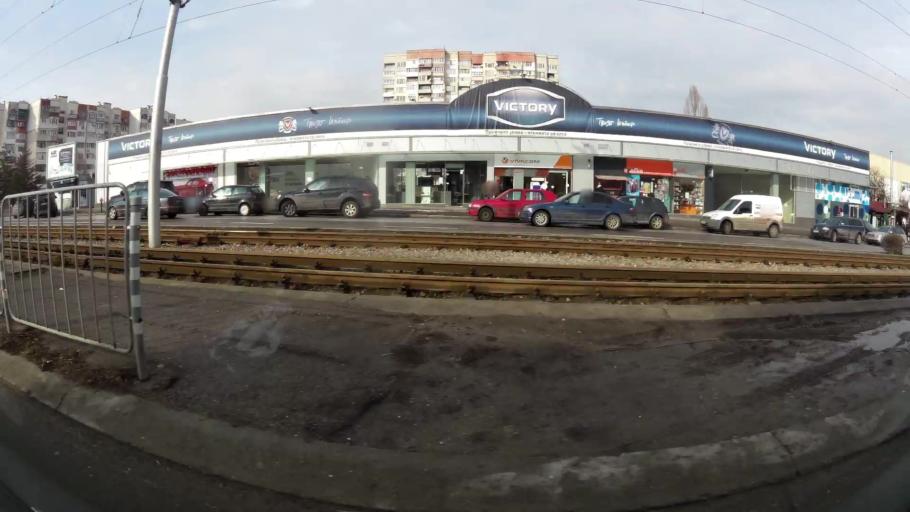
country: BG
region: Sofiya
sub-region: Obshtina Bozhurishte
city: Bozhurishte
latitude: 42.7132
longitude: 23.2486
